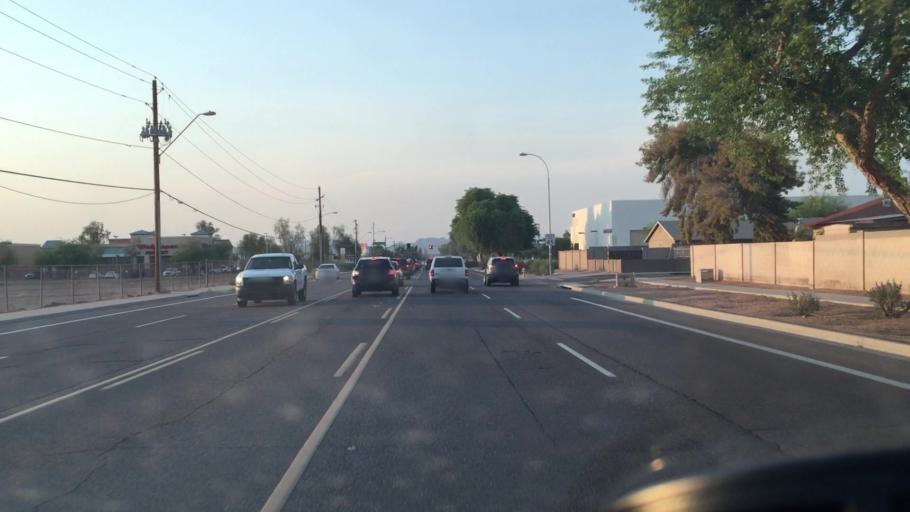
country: US
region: Arizona
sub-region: Maricopa County
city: Guadalupe
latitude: 33.3902
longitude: -111.9955
